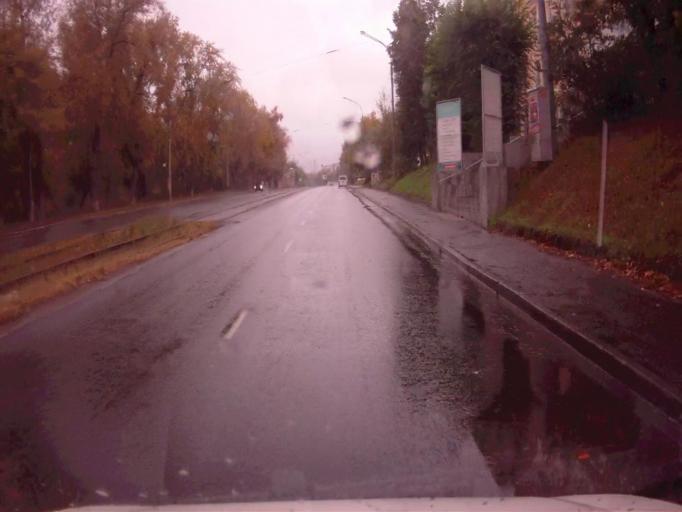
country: RU
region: Chelyabinsk
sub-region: Gorod Chelyabinsk
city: Chelyabinsk
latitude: 55.1809
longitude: 61.4146
